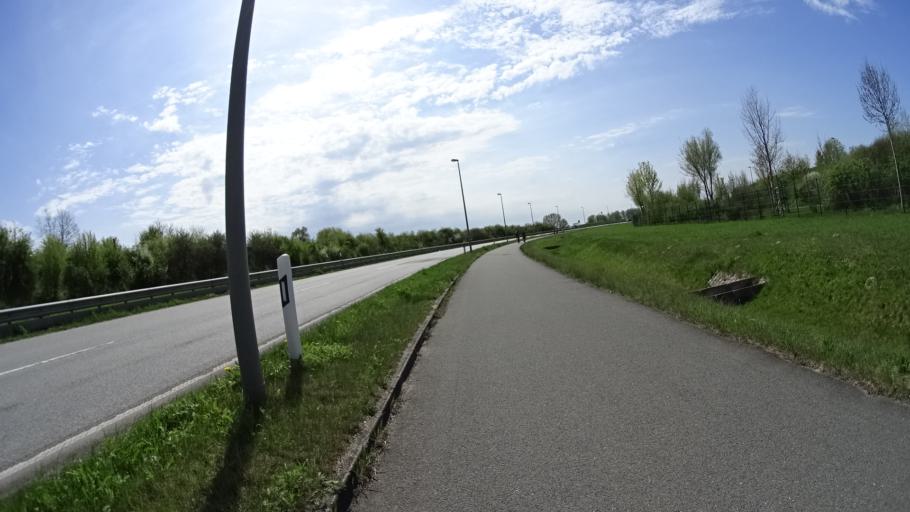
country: DE
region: Lower Saxony
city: Neu Wulmstorf
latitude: 53.5311
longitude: 9.8434
